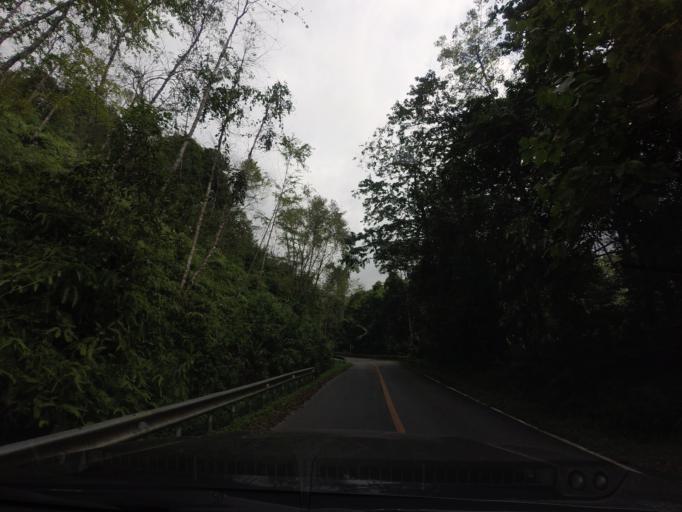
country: TH
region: Nan
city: Bo Kluea
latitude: 19.2060
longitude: 101.0713
